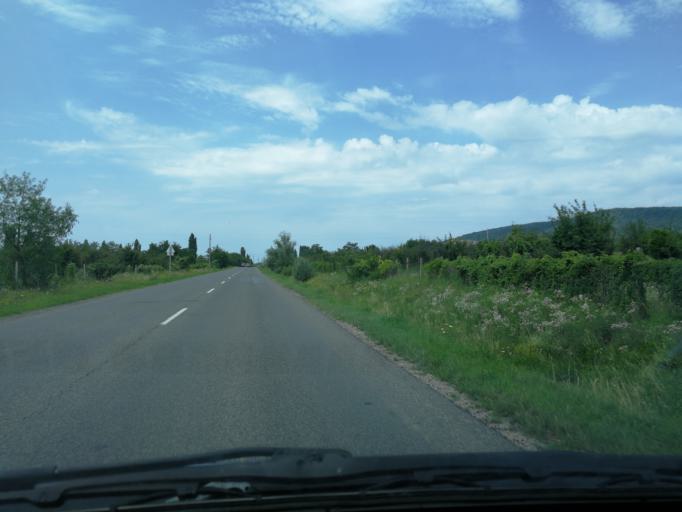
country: HU
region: Baranya
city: Siklos
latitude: 45.8676
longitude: 18.2881
